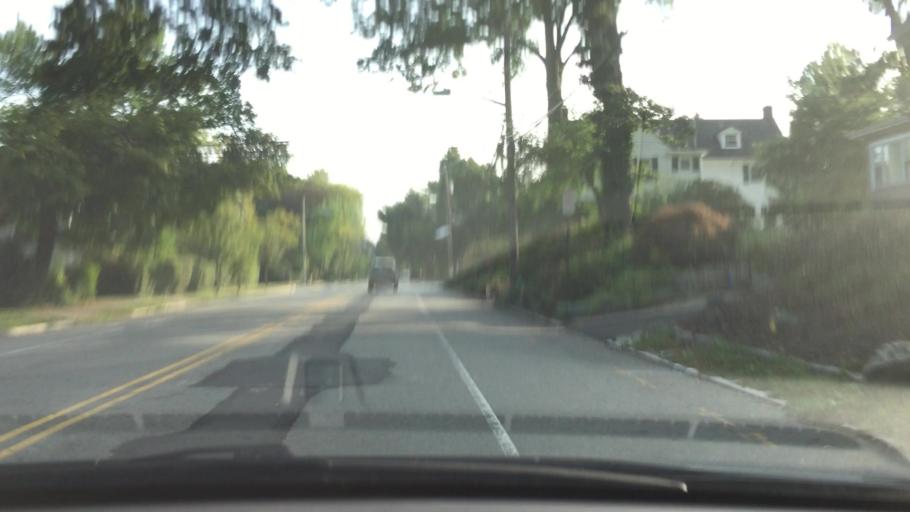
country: US
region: New Jersey
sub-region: Essex County
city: Montclair
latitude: 40.8314
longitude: -74.1974
